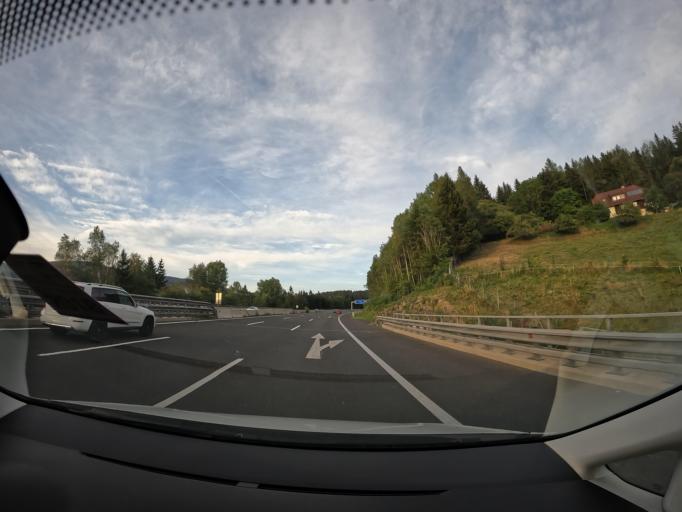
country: AT
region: Carinthia
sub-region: Politischer Bezirk Wolfsberg
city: Bad Sankt Leonhard im Lavanttal
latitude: 46.9407
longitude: 14.8338
